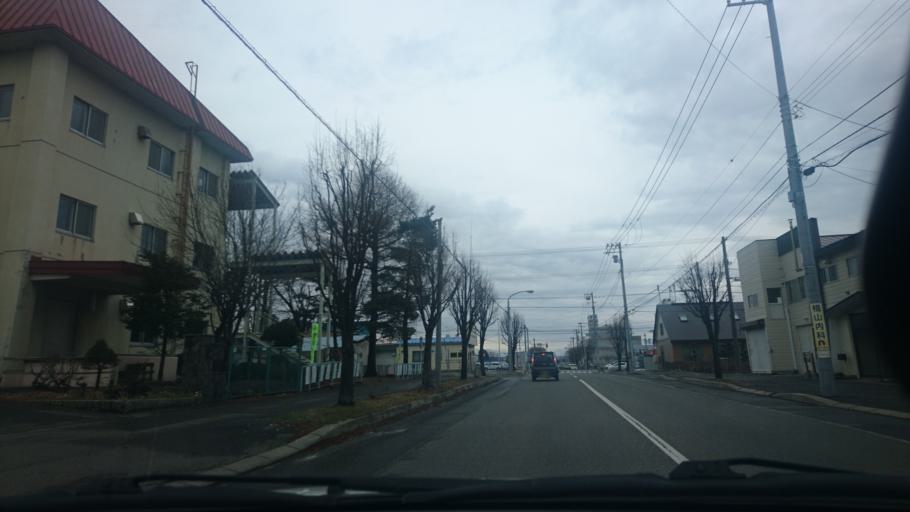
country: JP
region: Hokkaido
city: Obihiro
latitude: 42.9302
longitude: 143.1931
